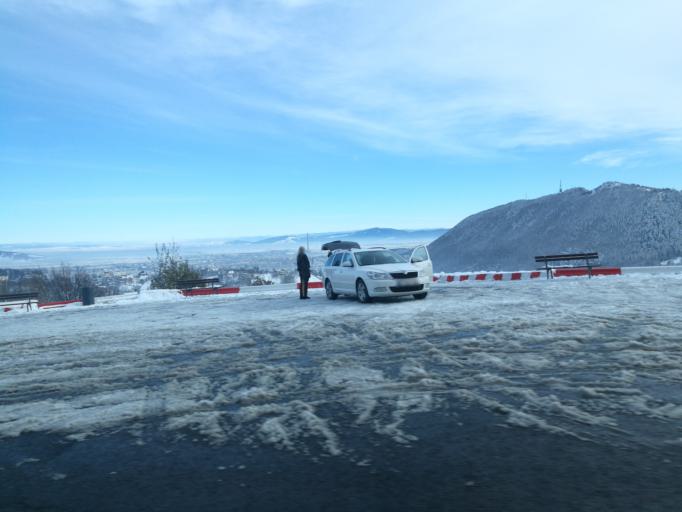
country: RO
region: Brasov
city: Brasov
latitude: 45.6362
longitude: 25.5647
